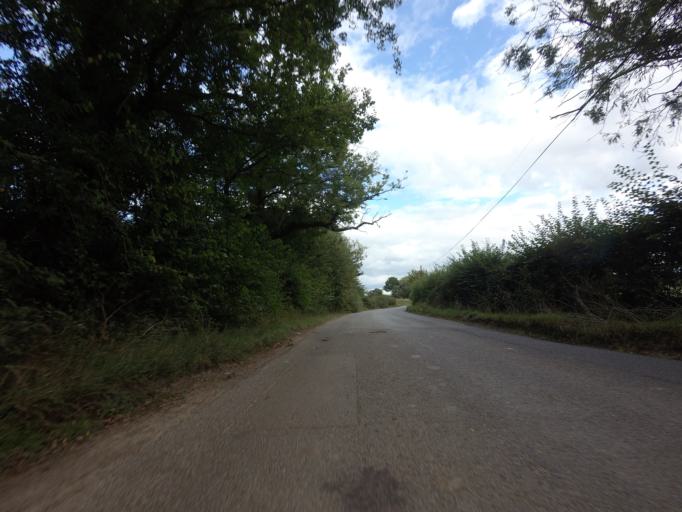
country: GB
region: England
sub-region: Kent
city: Marden
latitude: 51.2161
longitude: 0.4836
